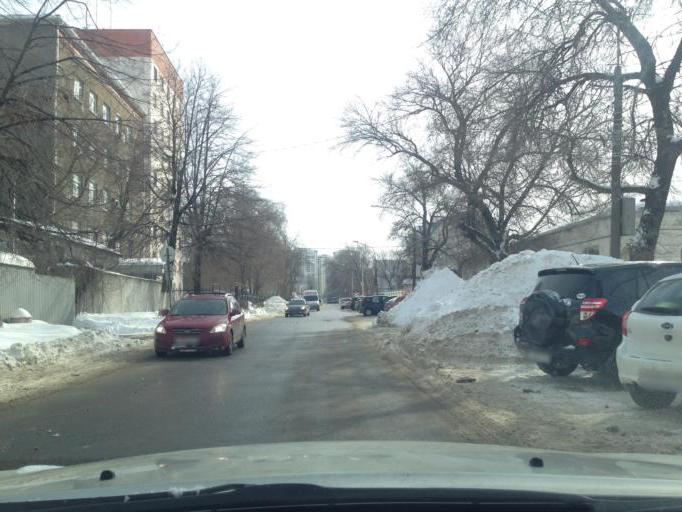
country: RU
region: Voronezj
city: Voronezh
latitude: 51.6619
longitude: 39.1725
